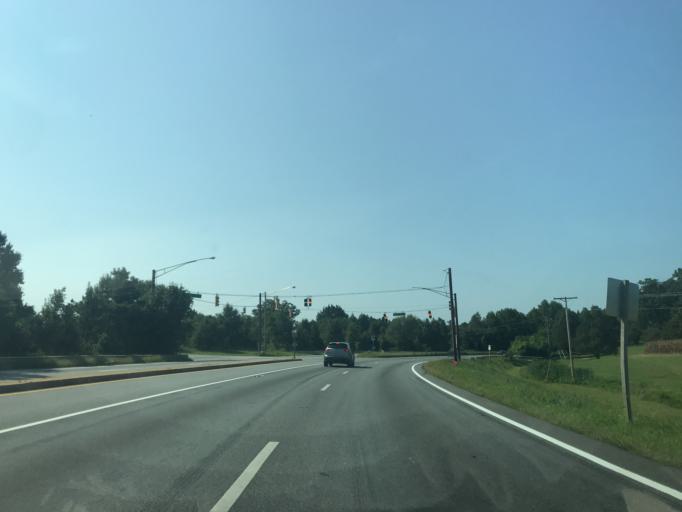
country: US
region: Maryland
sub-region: Charles County
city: Waldorf
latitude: 38.6185
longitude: -76.8750
